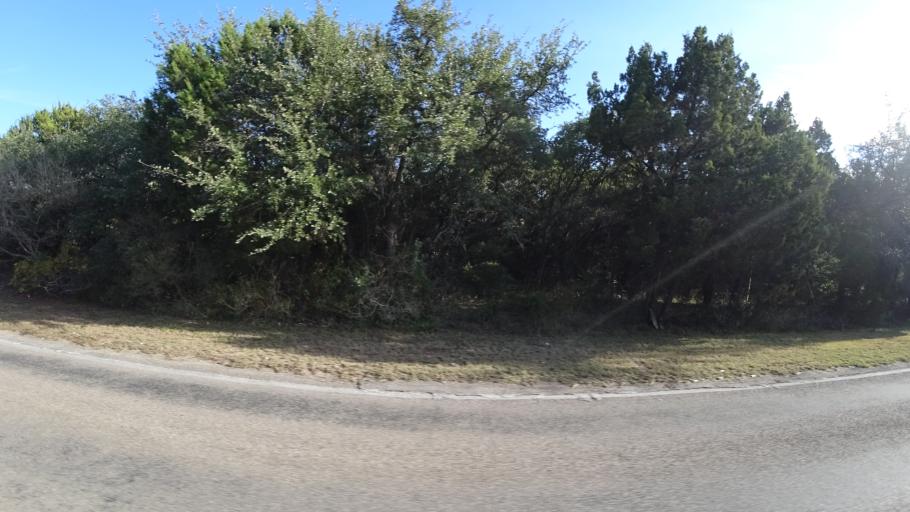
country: US
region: Texas
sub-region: Travis County
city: Bee Cave
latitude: 30.2466
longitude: -97.9317
